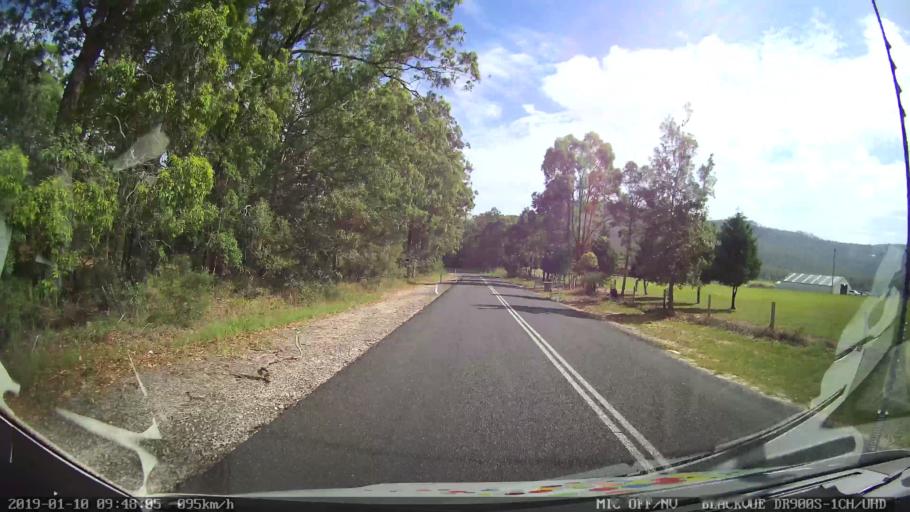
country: AU
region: New South Wales
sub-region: Coffs Harbour
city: Nana Glen
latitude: -30.0770
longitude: 152.9893
